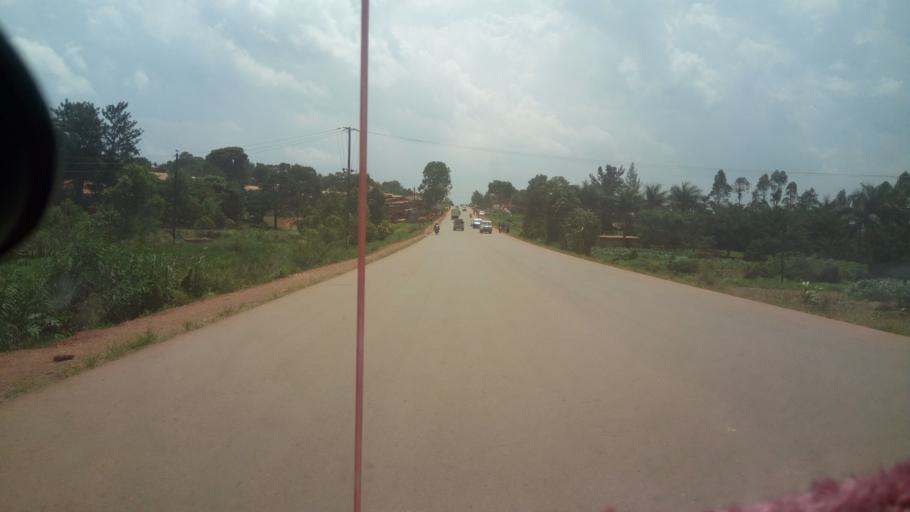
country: UG
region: Central Region
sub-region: Wakiso District
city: Wakiso
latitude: 0.3875
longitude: 32.5123
